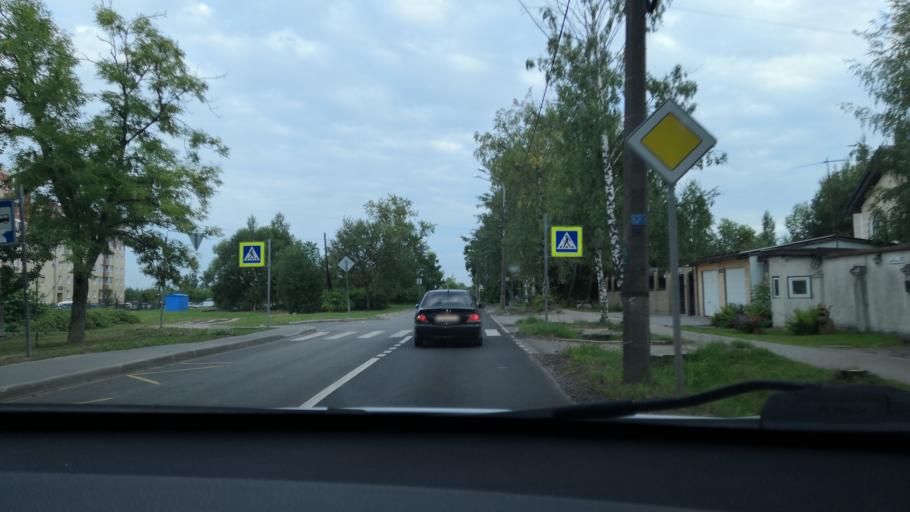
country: RU
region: St.-Petersburg
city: Pushkin
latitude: 59.6970
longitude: 30.4116
